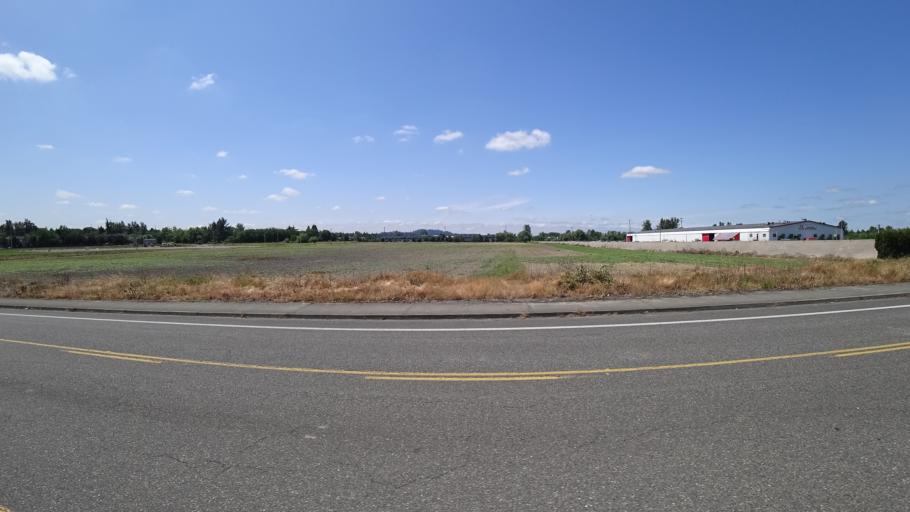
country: US
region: Oregon
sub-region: Multnomah County
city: Fairview
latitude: 45.5540
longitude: -122.5002
